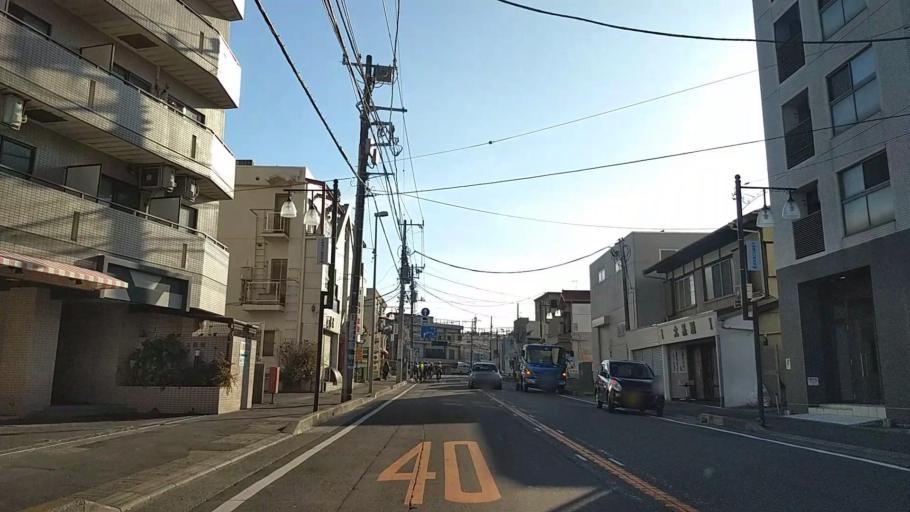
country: JP
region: Kanagawa
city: Fujisawa
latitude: 35.3112
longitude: 139.4881
